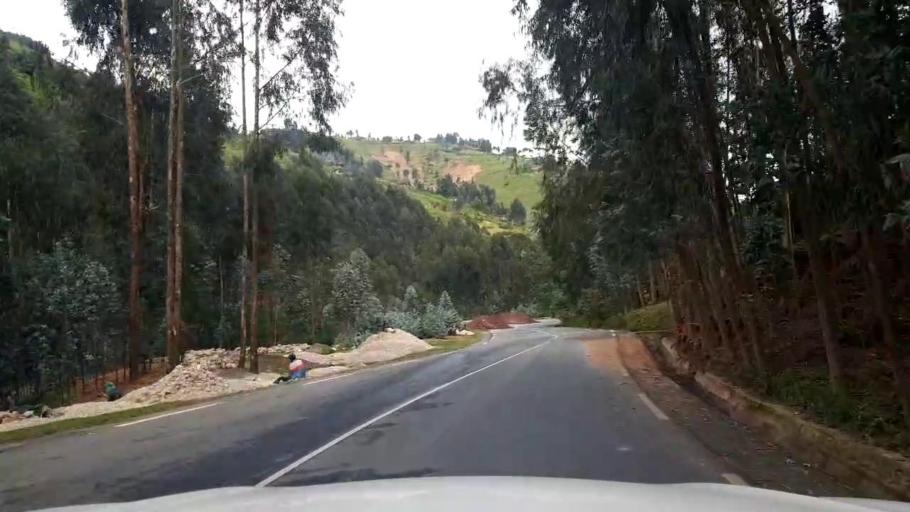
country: RW
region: Northern Province
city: Musanze
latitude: -1.6842
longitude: 29.5306
